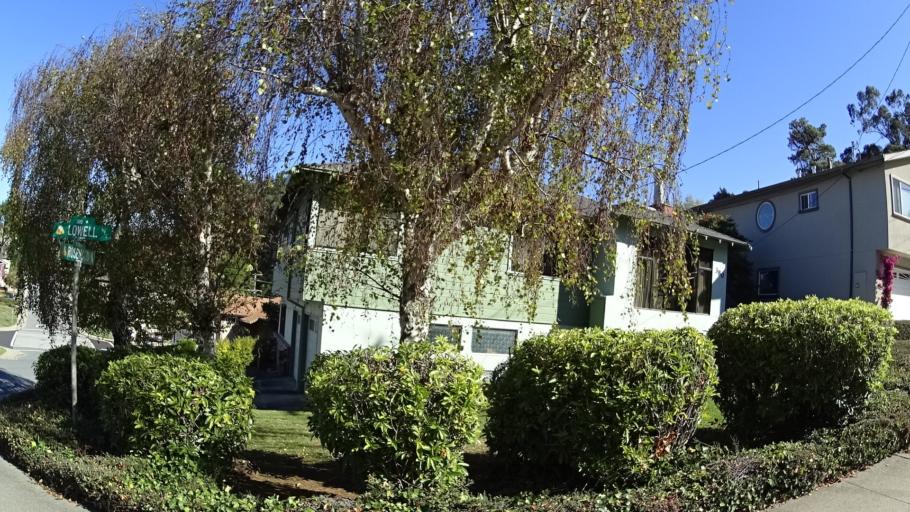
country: US
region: California
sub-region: San Mateo County
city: San Bruno
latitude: 37.6150
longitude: -122.4312
